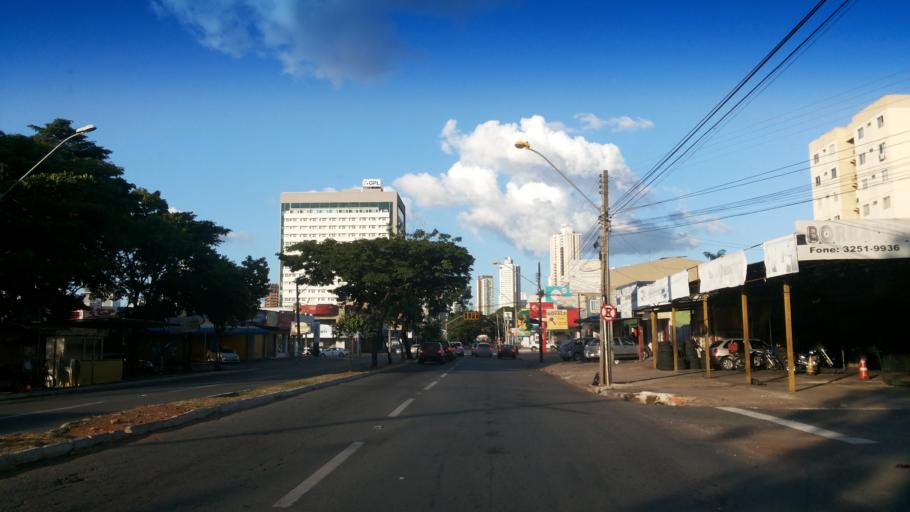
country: BR
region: Goias
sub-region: Goiania
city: Goiania
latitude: -16.7084
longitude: -49.2852
